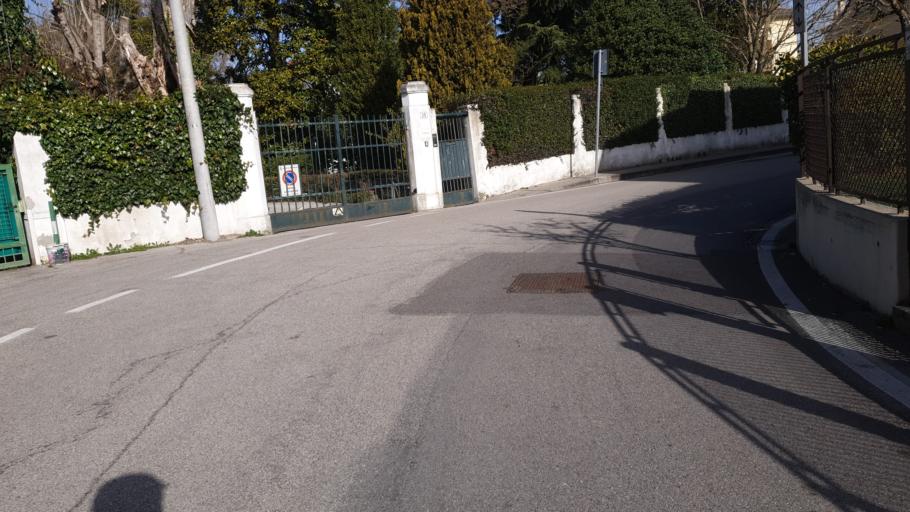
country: IT
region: Veneto
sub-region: Provincia di Padova
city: Noventa
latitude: 45.4246
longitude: 11.9433
